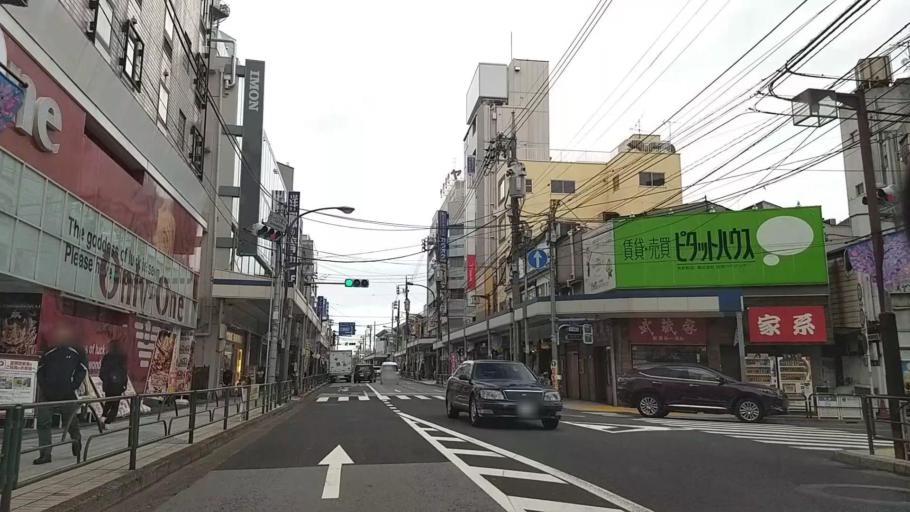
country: JP
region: Kanagawa
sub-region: Kawasaki-shi
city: Kawasaki
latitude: 35.6071
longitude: 139.7366
